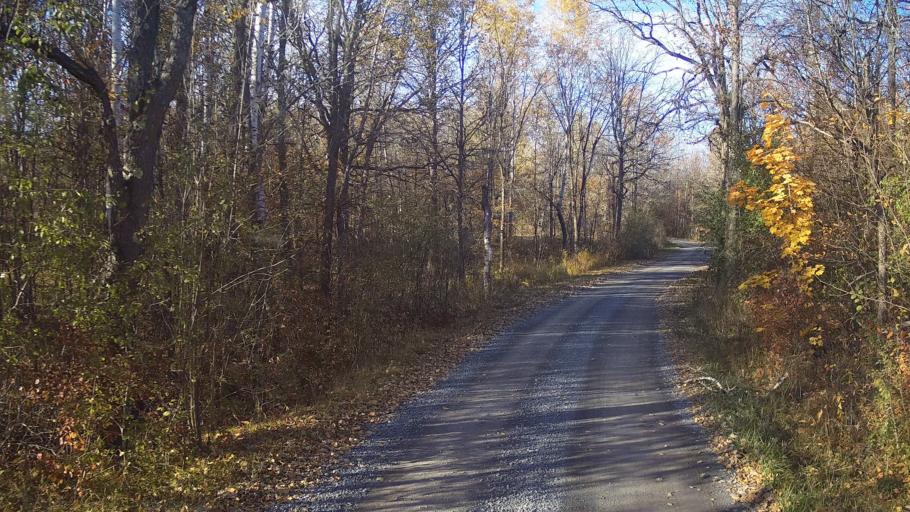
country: CA
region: Ontario
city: Perth
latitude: 44.7213
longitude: -76.4384
